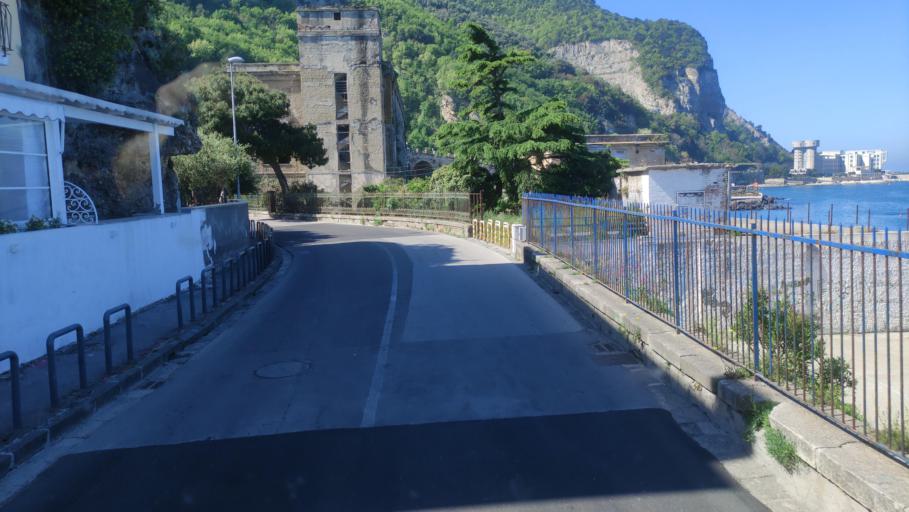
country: IT
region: Campania
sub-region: Provincia di Napoli
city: Castellammare di Stabia
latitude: 40.6903
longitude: 14.4582
